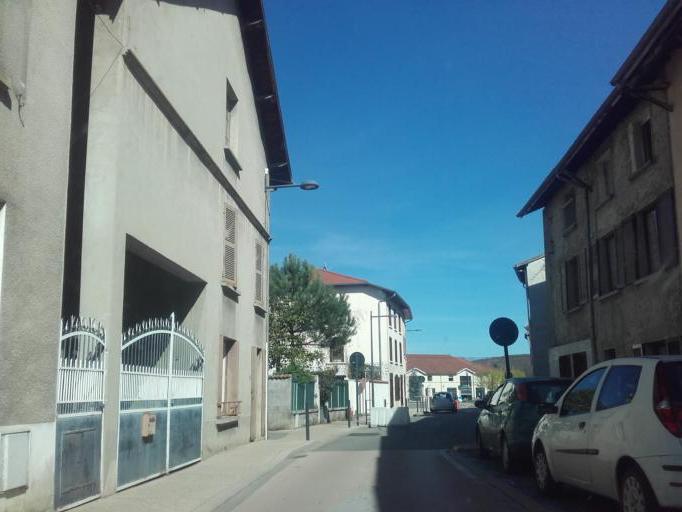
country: FR
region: Rhone-Alpes
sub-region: Departement de l'Isere
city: Saint-Etienne-de-Saint-Geoirs
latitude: 45.3389
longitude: 5.3466
